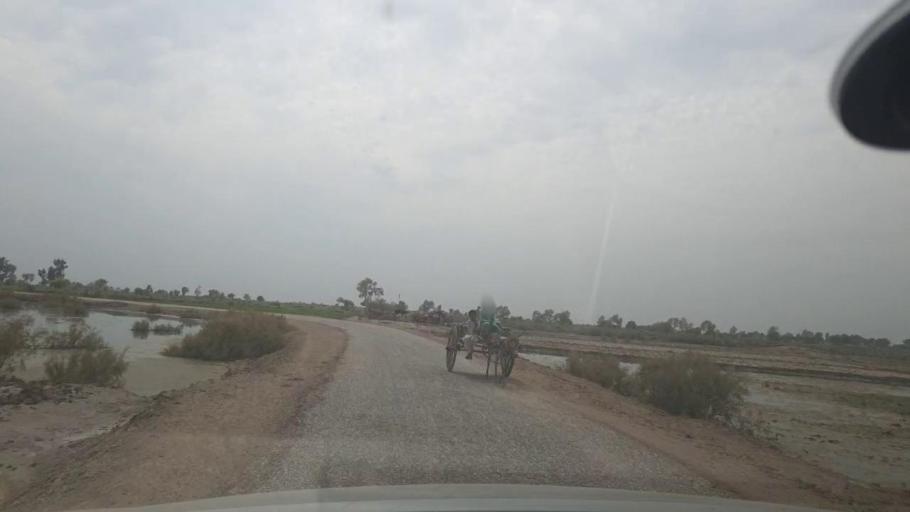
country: PK
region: Balochistan
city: Mehrabpur
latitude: 28.0542
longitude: 68.1366
